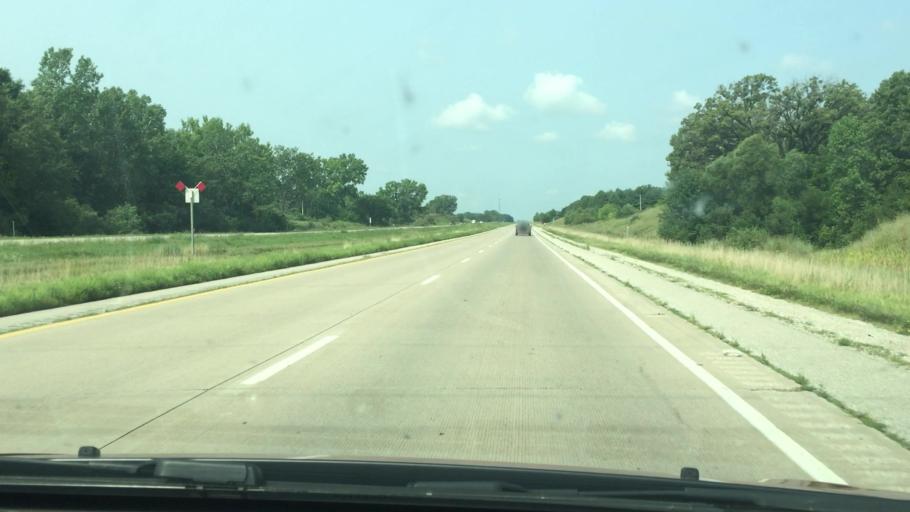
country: US
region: Iowa
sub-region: Scott County
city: Blue Grass
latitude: 41.5154
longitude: -90.8238
